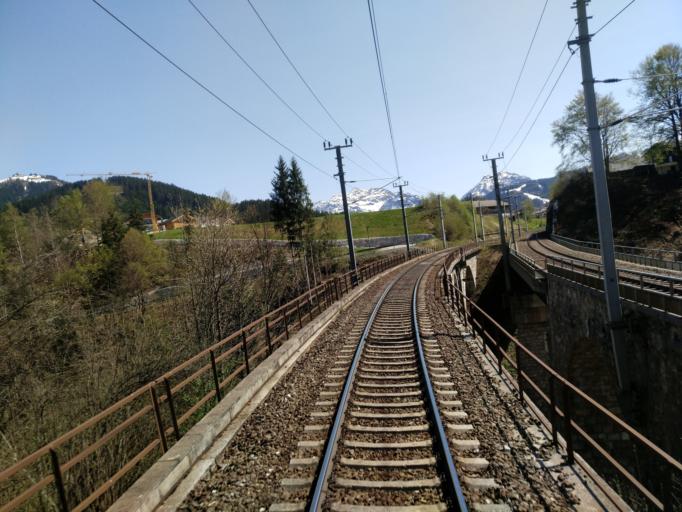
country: AT
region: Tyrol
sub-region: Politischer Bezirk Kitzbuhel
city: Fieberbrunn
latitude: 47.4891
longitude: 12.5353
